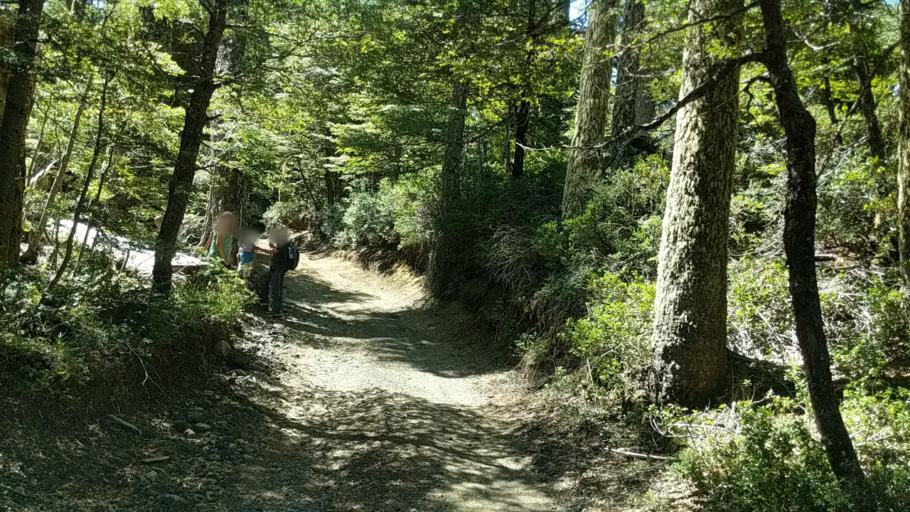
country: CL
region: Araucania
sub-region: Provincia de Cautin
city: Pucon
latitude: -39.4628
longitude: -71.8513
